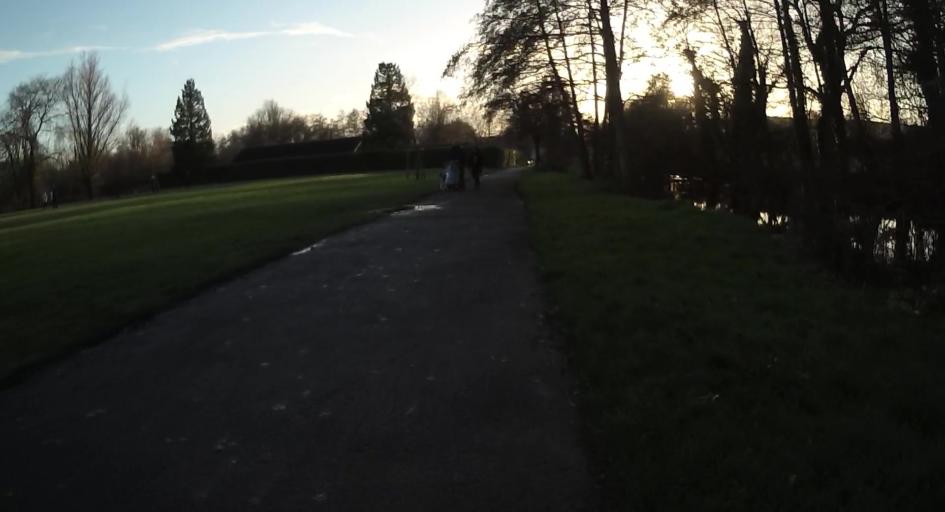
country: GB
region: England
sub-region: Hampshire
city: Winchester
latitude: 51.0678
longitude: -1.3089
